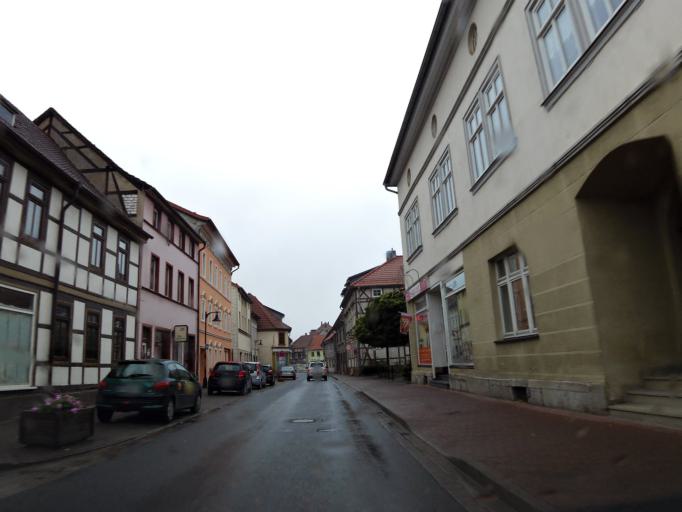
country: DE
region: Thuringia
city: Ellrich
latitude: 51.5876
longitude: 10.6642
